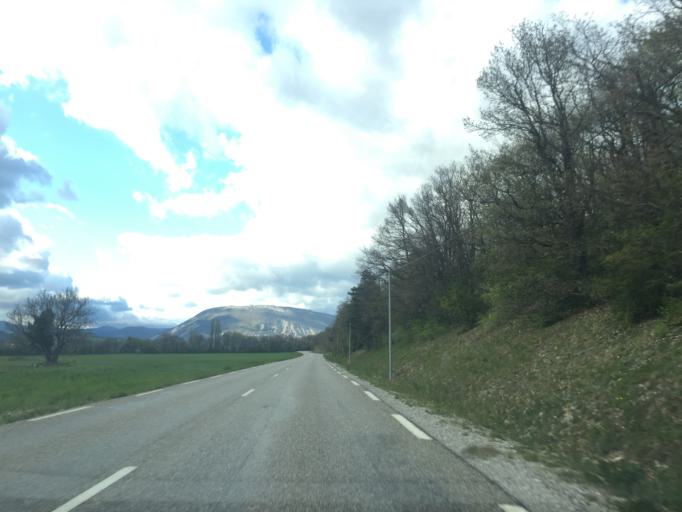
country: FR
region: Provence-Alpes-Cote d'Azur
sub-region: Departement des Hautes-Alpes
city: Serres
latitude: 44.4548
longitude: 5.7255
